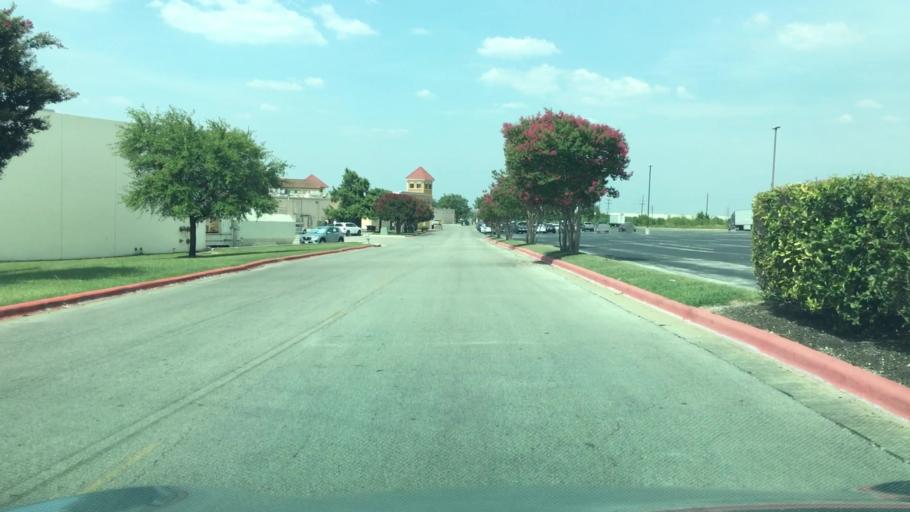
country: US
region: Texas
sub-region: Hays County
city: San Marcos
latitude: 29.8254
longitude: -97.9824
